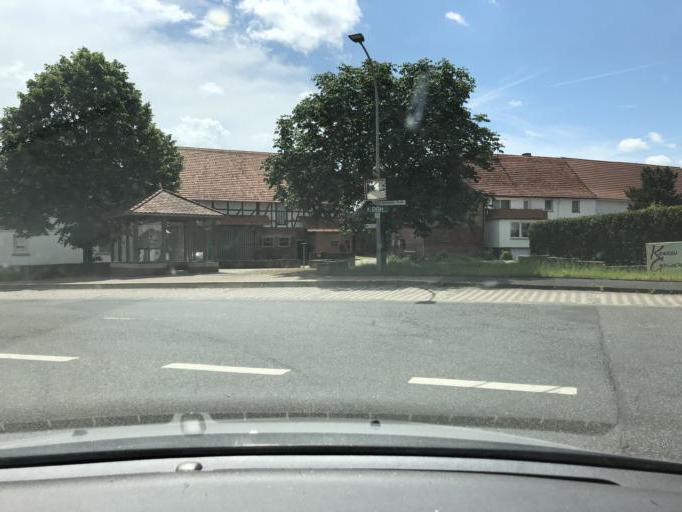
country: DE
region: Hesse
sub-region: Regierungsbezirk Kassel
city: Alheim
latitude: 51.0411
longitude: 9.6545
